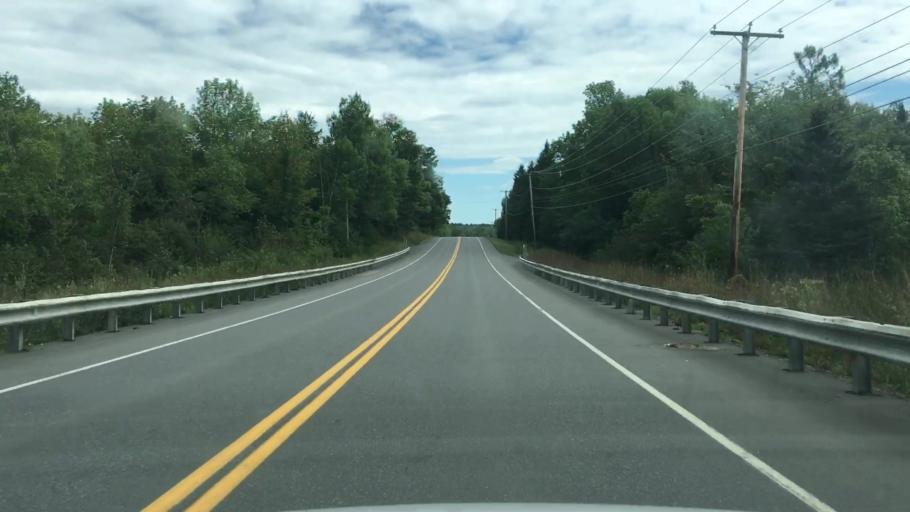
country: US
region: Maine
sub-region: Piscataquis County
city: Milo
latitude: 45.2407
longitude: -69.0425
